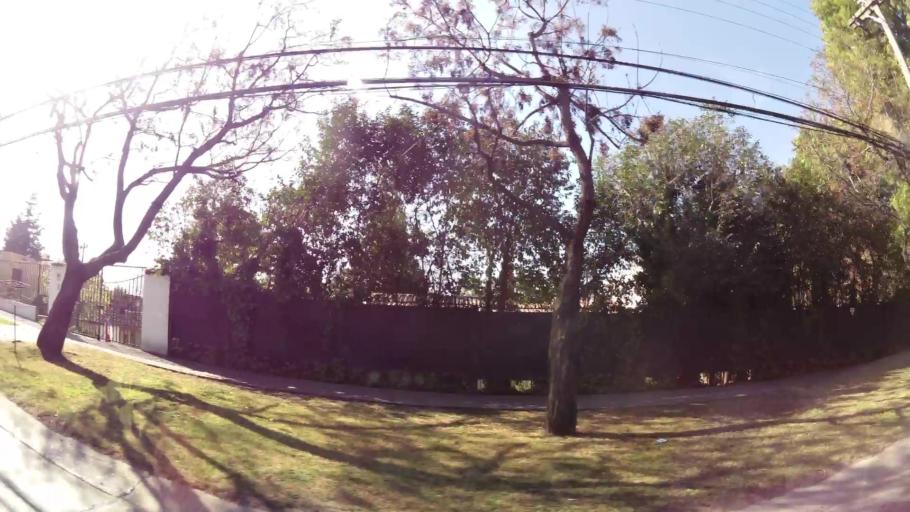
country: CL
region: Santiago Metropolitan
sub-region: Provincia de Santiago
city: Villa Presidente Frei, Nunoa, Santiago, Chile
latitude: -33.4032
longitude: -70.5232
